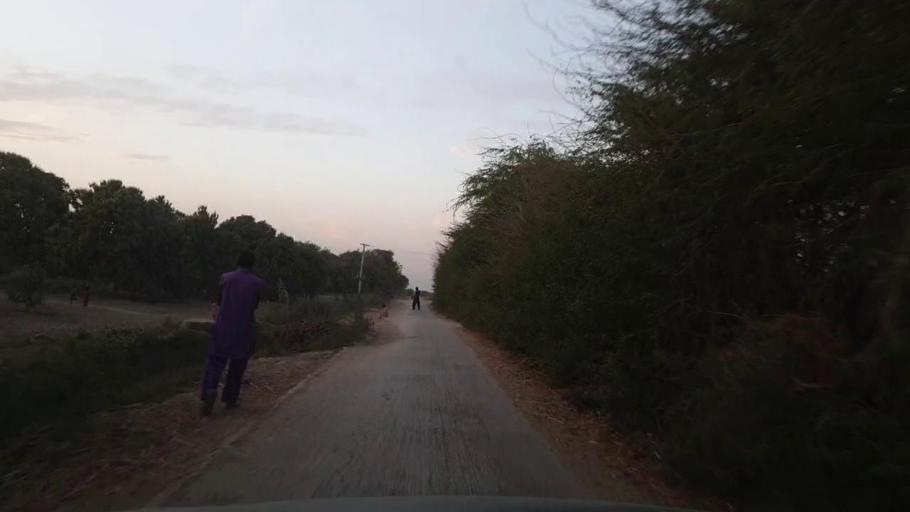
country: PK
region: Sindh
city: Kunri
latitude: 25.1460
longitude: 69.5576
